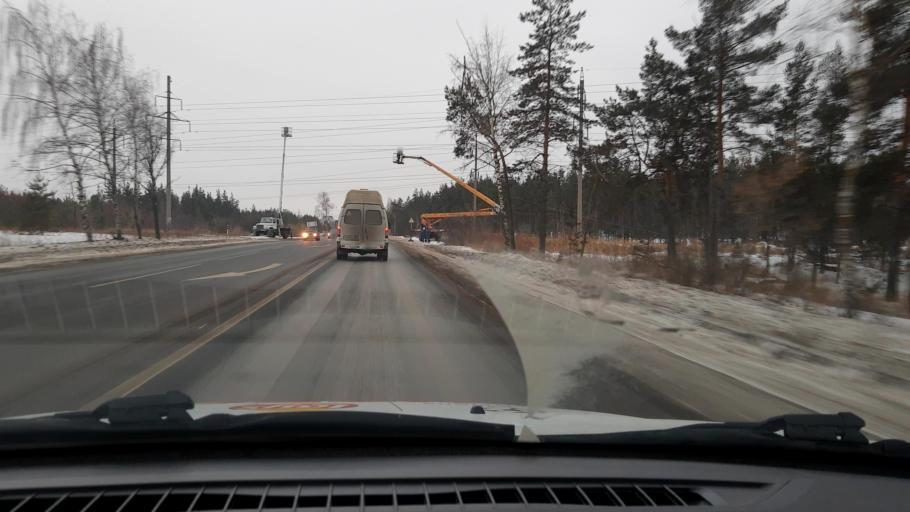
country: RU
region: Nizjnij Novgorod
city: Dzerzhinsk
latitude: 56.2680
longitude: 43.4714
